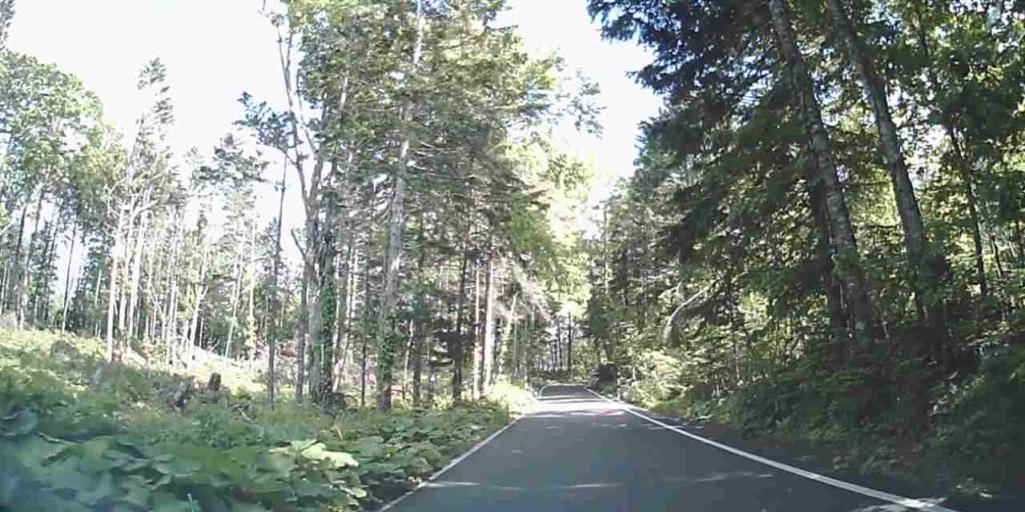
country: JP
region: Hokkaido
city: Shiraoi
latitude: 42.7390
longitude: 141.4104
